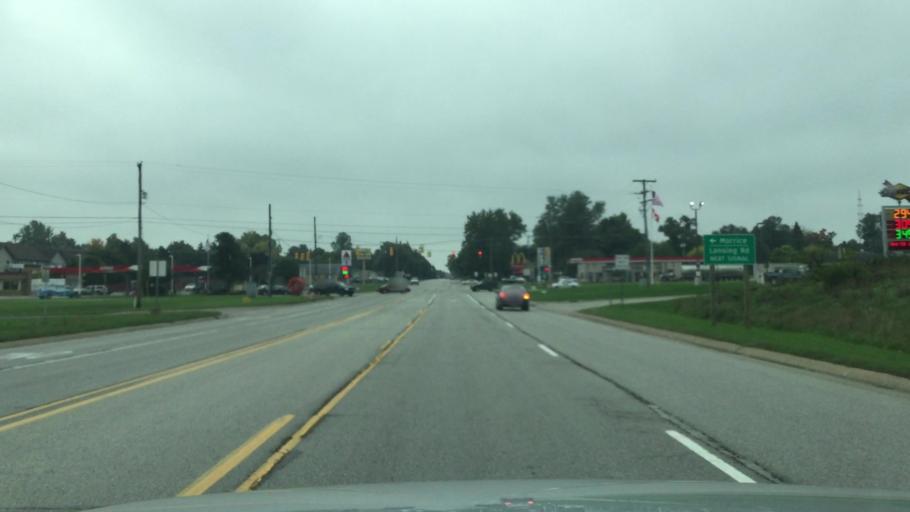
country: US
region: Michigan
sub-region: Shiawassee County
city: Perry
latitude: 42.8372
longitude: -84.2197
